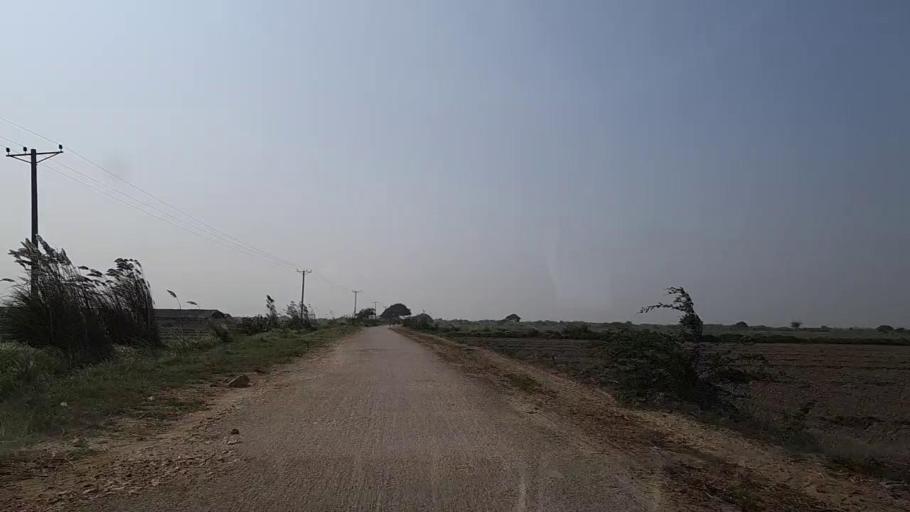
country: PK
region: Sindh
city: Mirpur Sakro
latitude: 24.5289
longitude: 67.5546
